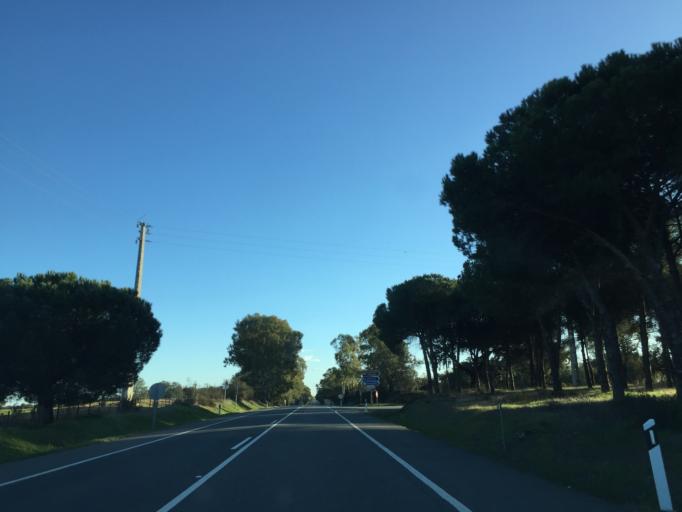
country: PT
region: Setubal
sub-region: Grandola
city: Grandola
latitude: 38.0352
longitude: -8.4006
